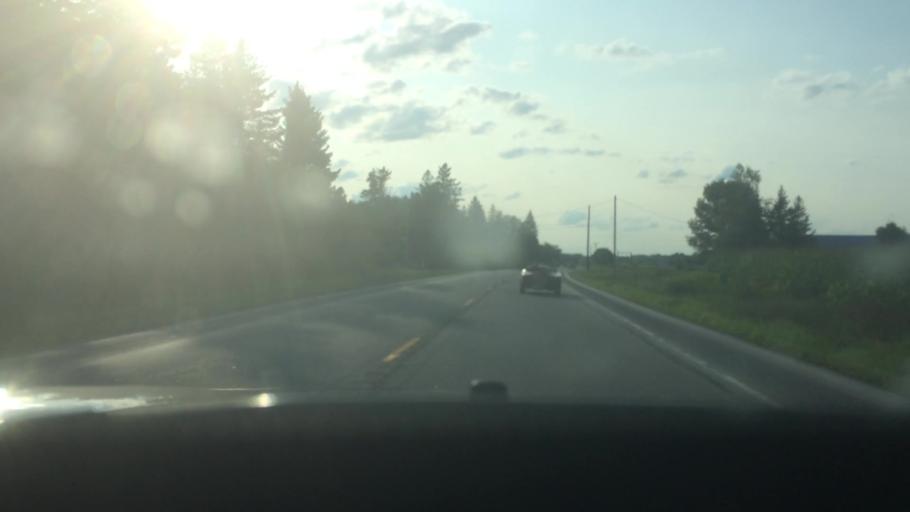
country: US
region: New York
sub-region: St. Lawrence County
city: Ogdensburg
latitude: 44.6579
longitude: -75.3253
